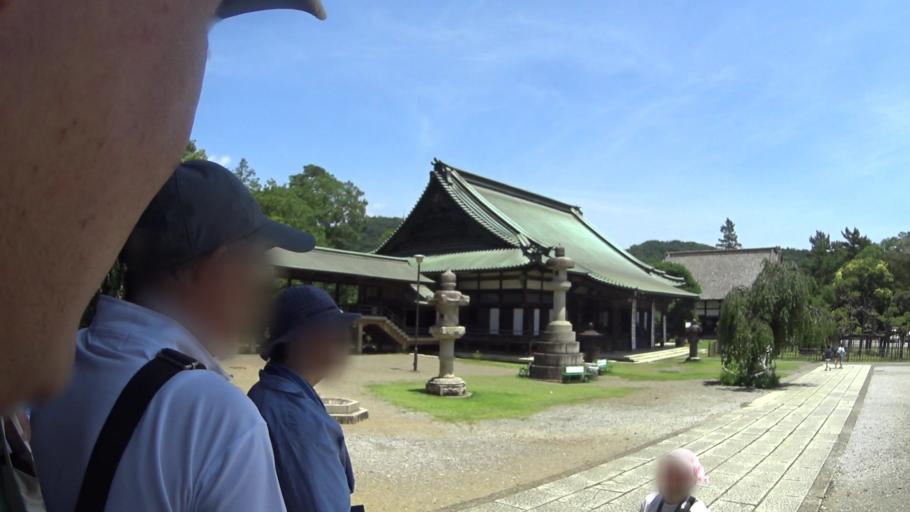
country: JP
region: Gunma
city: Ota
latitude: 36.3056
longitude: 139.3697
